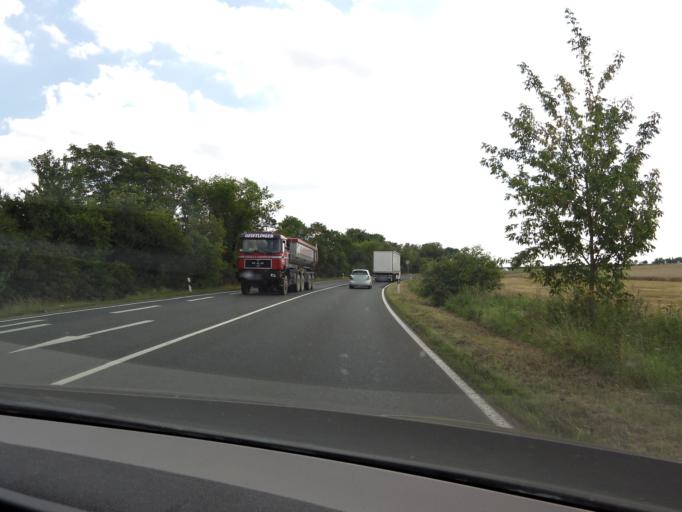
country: DE
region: Saxony-Anhalt
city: Magdeburg
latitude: 52.0784
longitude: 11.6181
